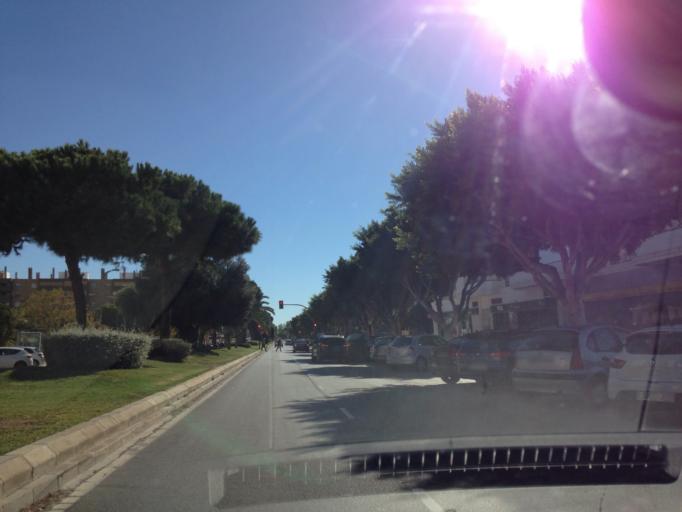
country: ES
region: Andalusia
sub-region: Provincia de Malaga
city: Malaga
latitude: 36.6901
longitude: -4.4562
